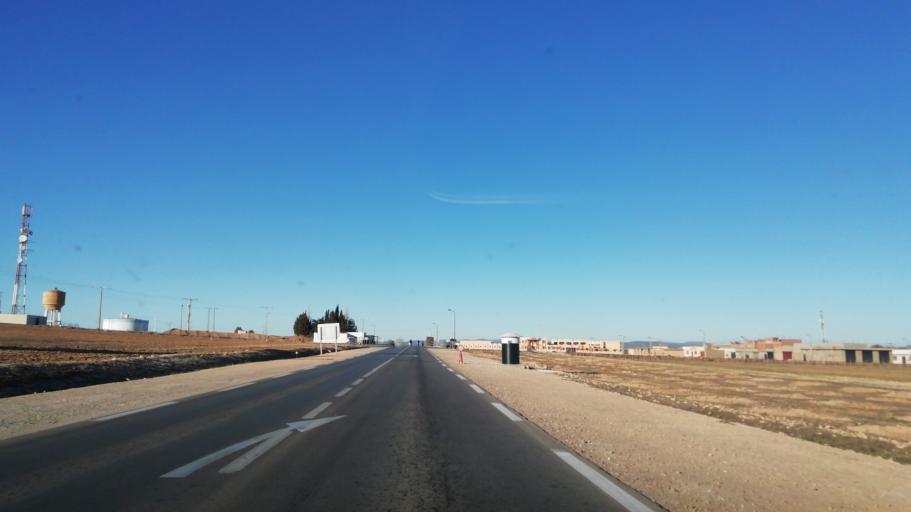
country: DZ
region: Tlemcen
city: Sebdou
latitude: 34.4773
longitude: -1.2711
